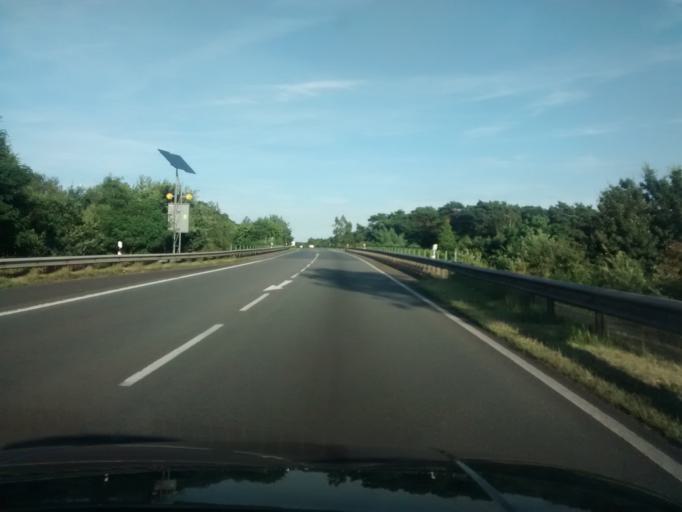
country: DE
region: Lower Saxony
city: Meppen
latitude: 52.7119
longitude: 7.3001
